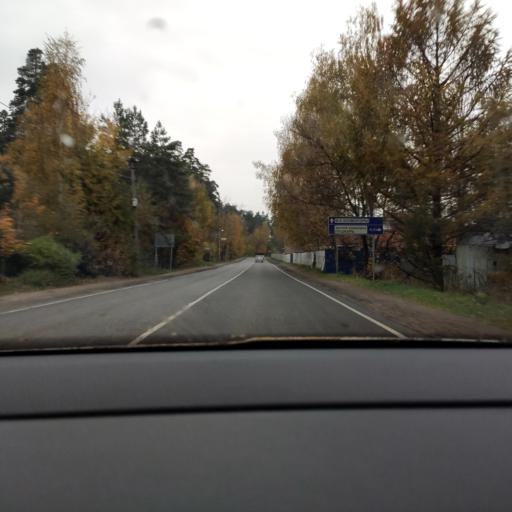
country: RU
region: Moskovskaya
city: Lesnyye Polyany
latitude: 55.9718
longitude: 37.8694
